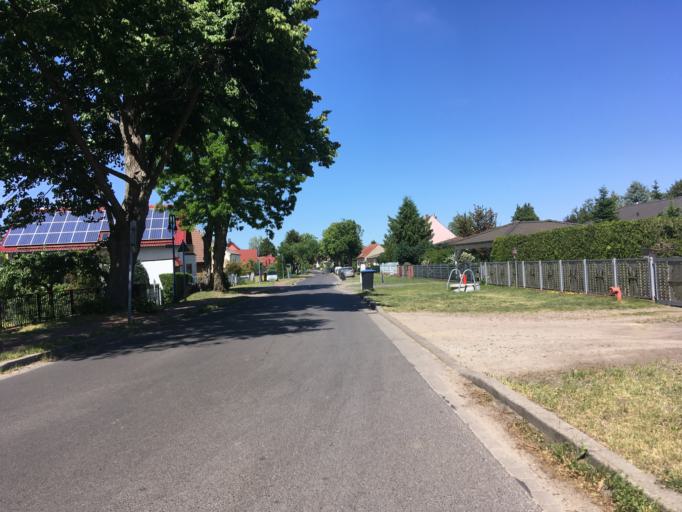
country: DE
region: Berlin
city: Muggelheim
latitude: 52.3893
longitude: 13.7037
